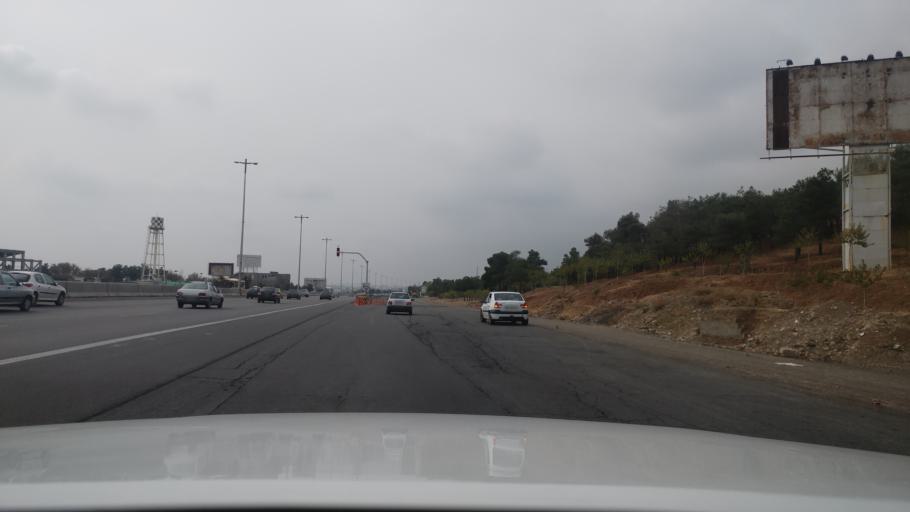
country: IR
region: Tehran
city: Shahr-e Qods
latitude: 35.7183
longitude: 51.2227
